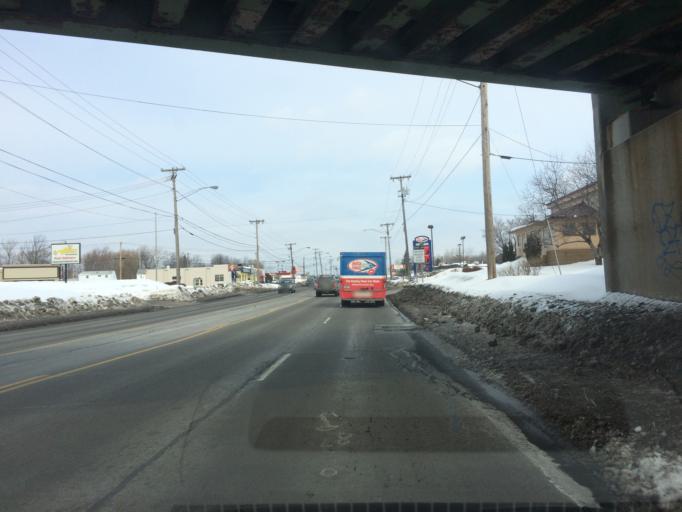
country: US
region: New York
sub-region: Monroe County
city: Rochester
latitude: 43.0918
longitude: -77.6342
